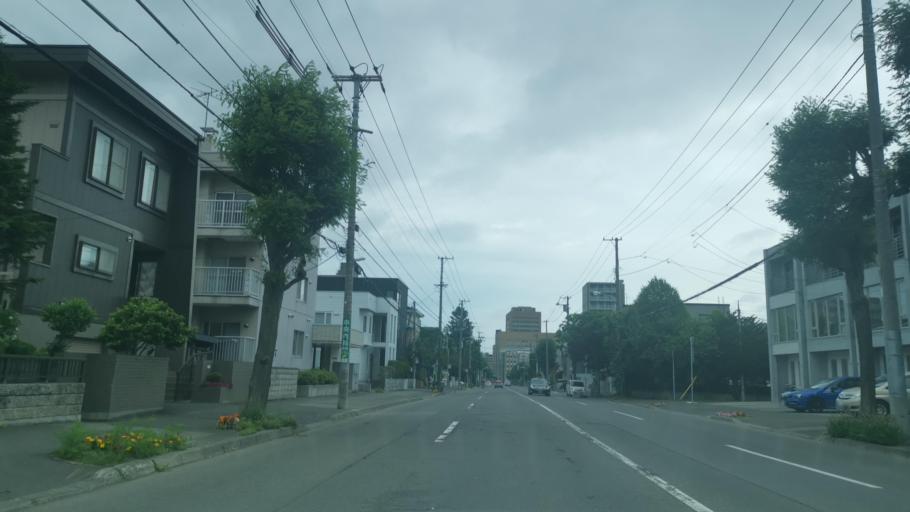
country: JP
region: Hokkaido
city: Sapporo
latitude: 43.0490
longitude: 141.3319
